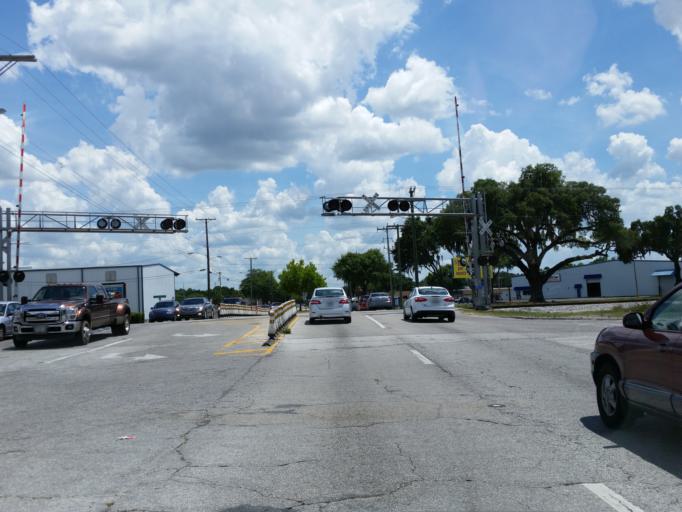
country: US
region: Florida
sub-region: Hillsborough County
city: Plant City
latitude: 28.0082
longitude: -82.1379
